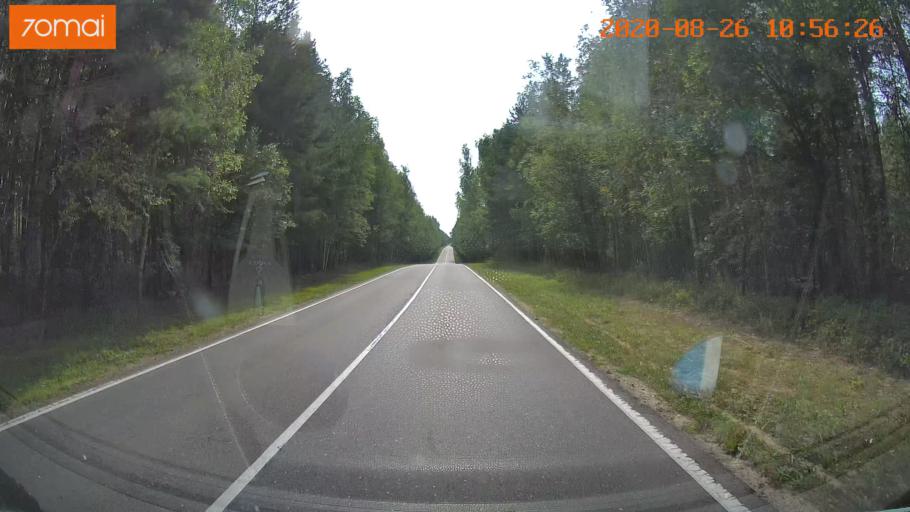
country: RU
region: Rjazan
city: Izhevskoye
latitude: 54.6032
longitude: 41.1871
